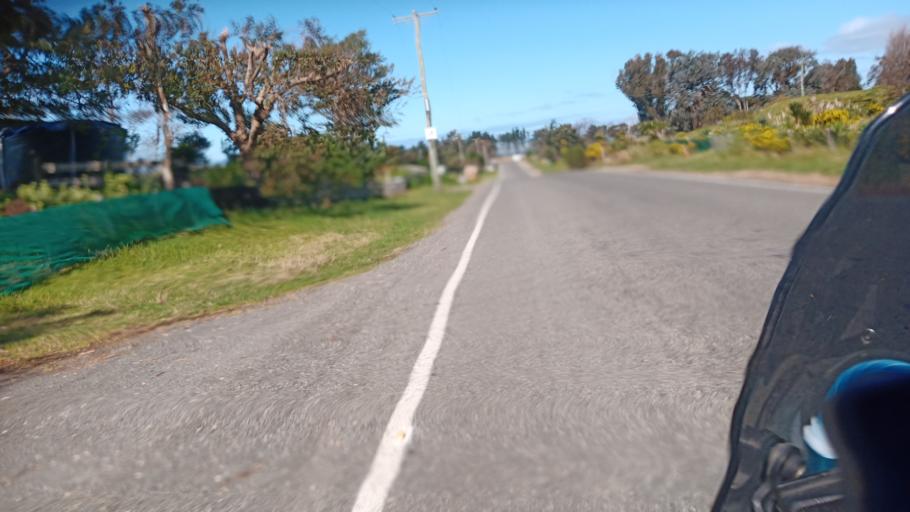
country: NZ
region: Gisborne
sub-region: Gisborne District
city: Gisborne
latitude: -39.0158
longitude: 177.8801
